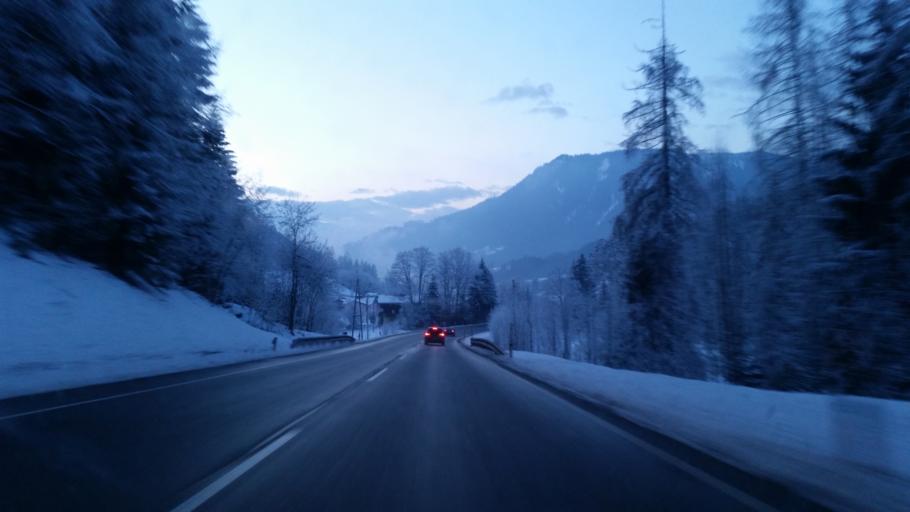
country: AT
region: Salzburg
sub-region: Politischer Bezirk Sankt Johann im Pongau
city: Eben im Pongau
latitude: 47.4184
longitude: 13.3752
